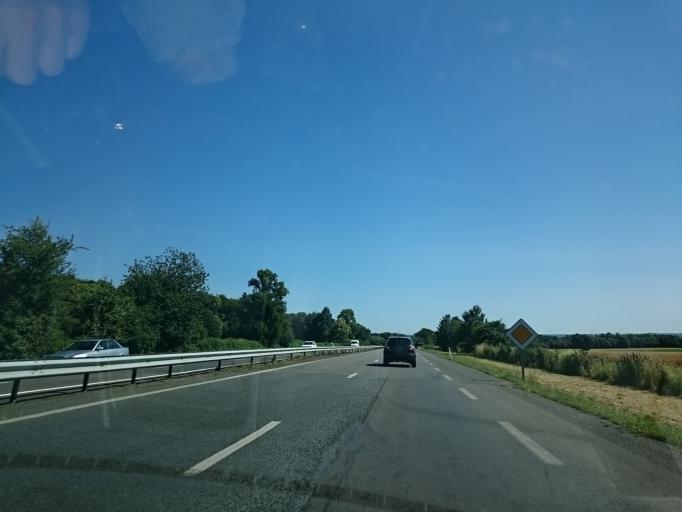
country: FR
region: Brittany
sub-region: Departement d'Ille-et-Vilaine
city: Saint-Pierre-de-Plesguen
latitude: 48.4243
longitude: -1.9120
